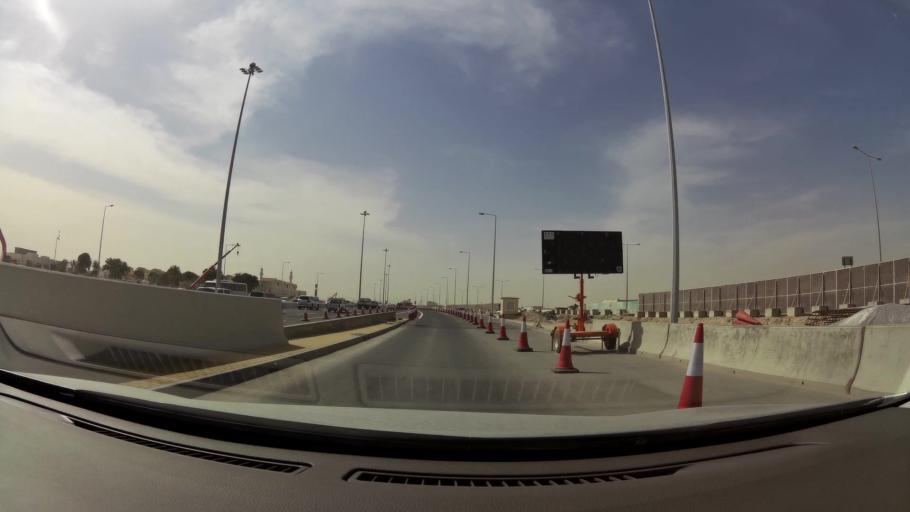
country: QA
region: Baladiyat ar Rayyan
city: Ar Rayyan
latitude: 25.3039
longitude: 51.4190
